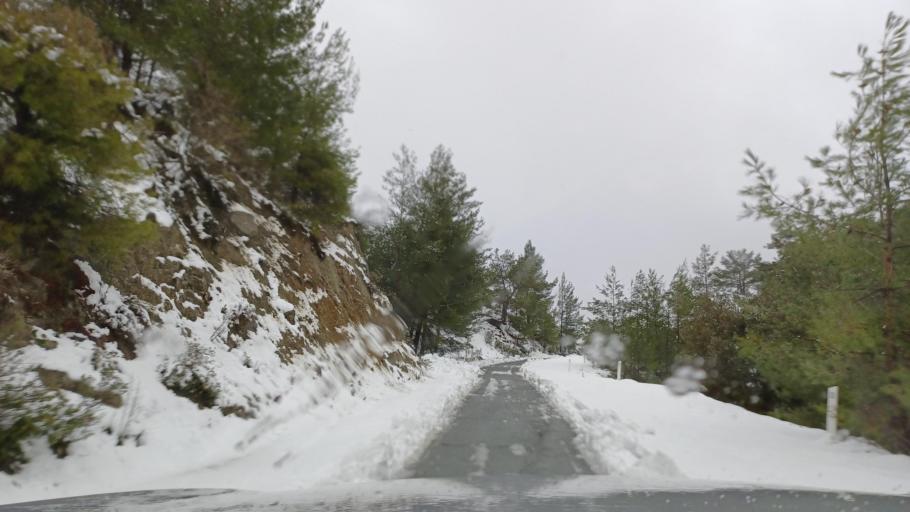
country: CY
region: Limassol
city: Pelendri
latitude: 34.9094
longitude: 32.9575
